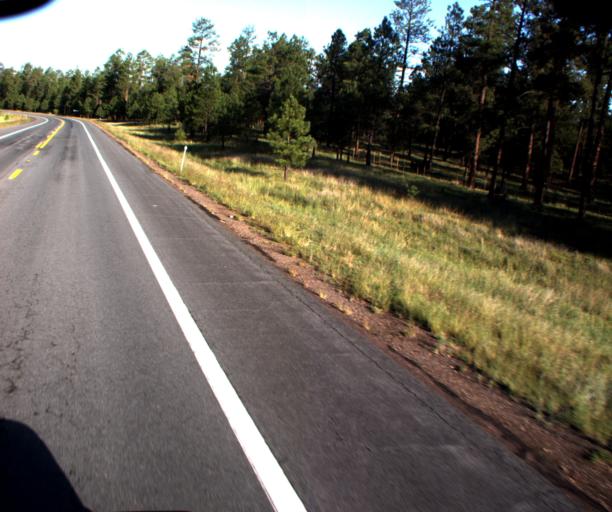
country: US
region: New Mexico
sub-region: Catron County
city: Reserve
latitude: 33.8129
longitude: -109.0561
